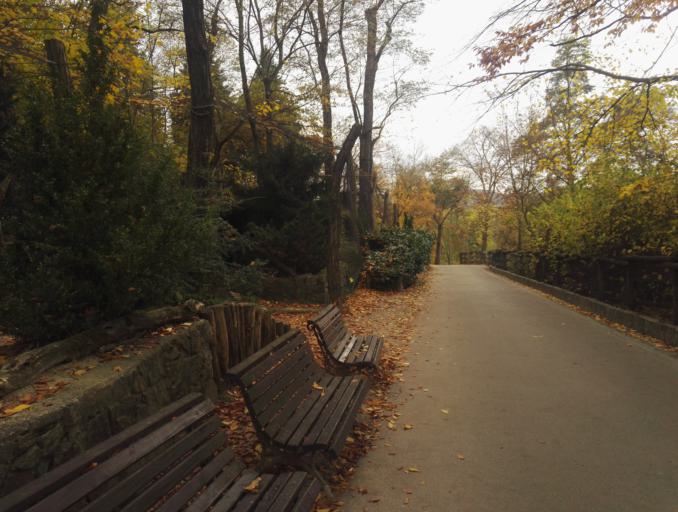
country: CZ
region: Praha
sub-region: Praha 1
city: Mala Strana
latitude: 50.1195
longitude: 14.4043
